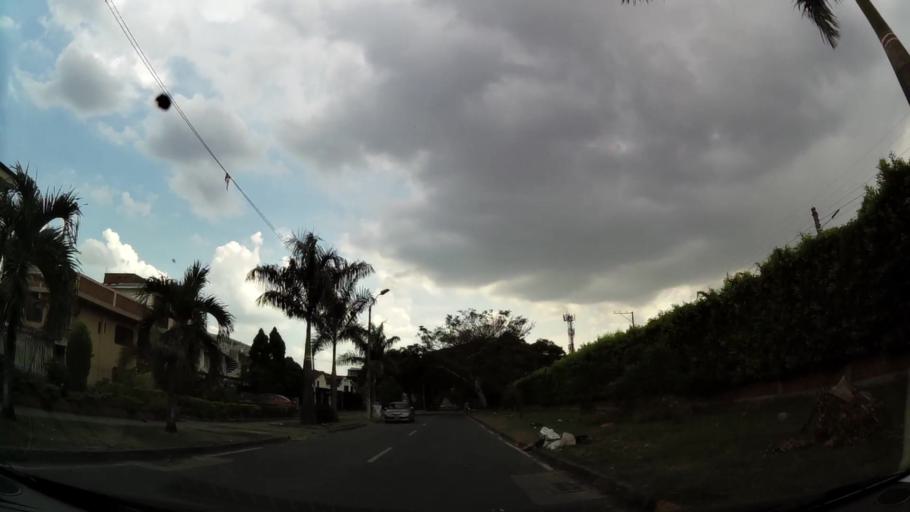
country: CO
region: Valle del Cauca
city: Cali
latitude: 3.4553
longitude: -76.4898
